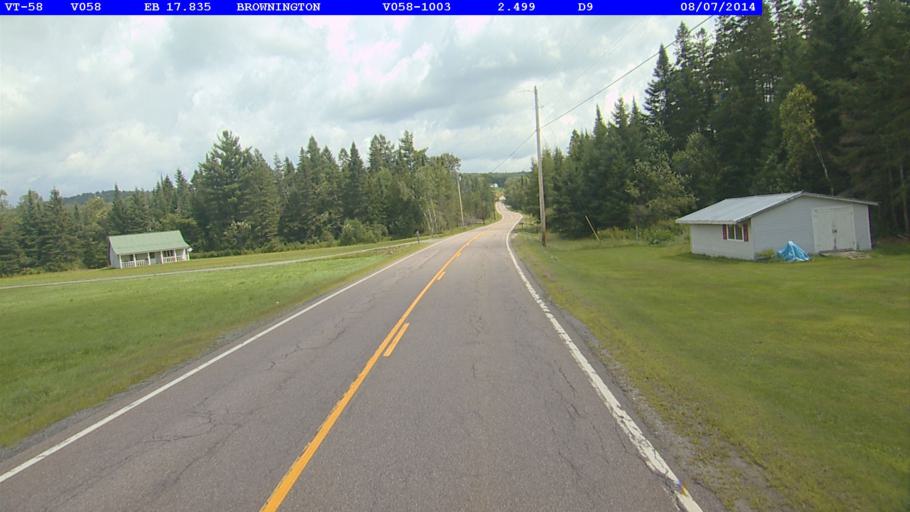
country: US
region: Vermont
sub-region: Orleans County
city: Newport
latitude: 44.7952
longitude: -72.0986
